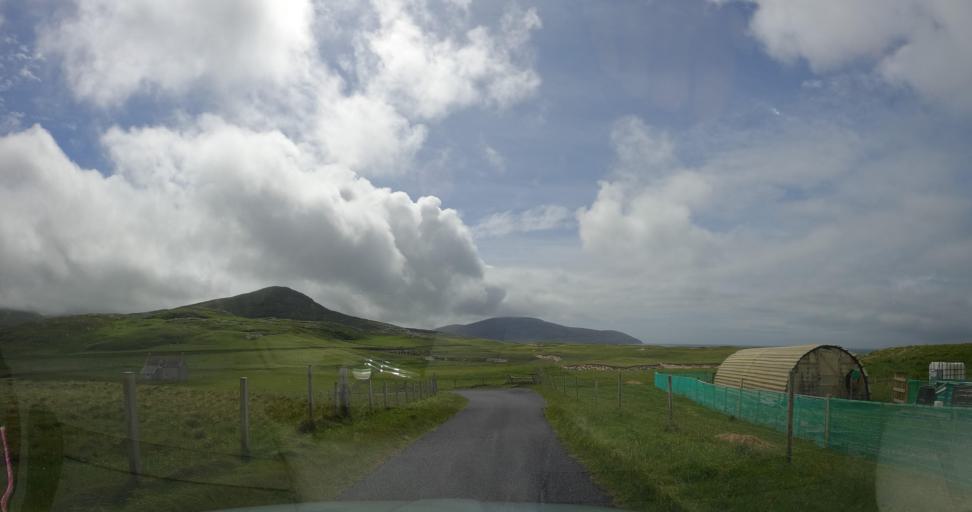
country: GB
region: Scotland
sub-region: Eilean Siar
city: Barra
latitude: 57.0057
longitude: -7.4995
